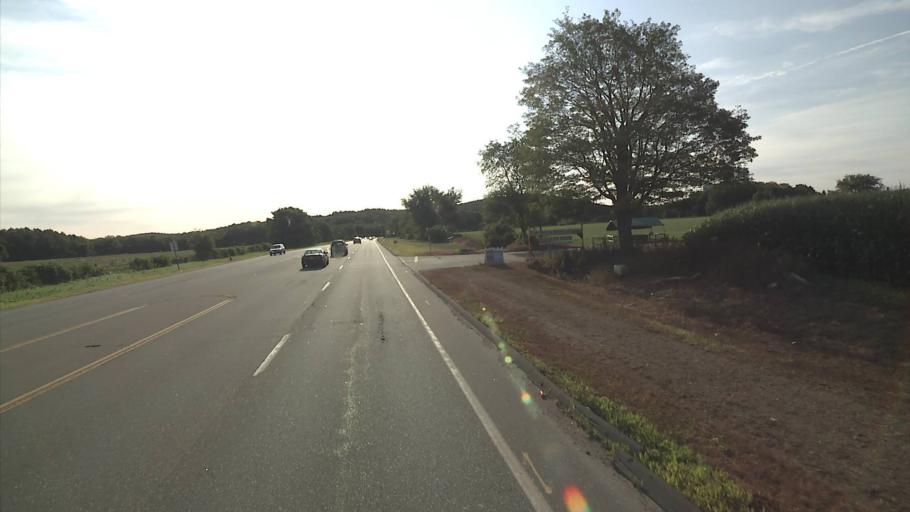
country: US
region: Connecticut
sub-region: New London County
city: Preston City
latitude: 41.4882
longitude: -71.9813
